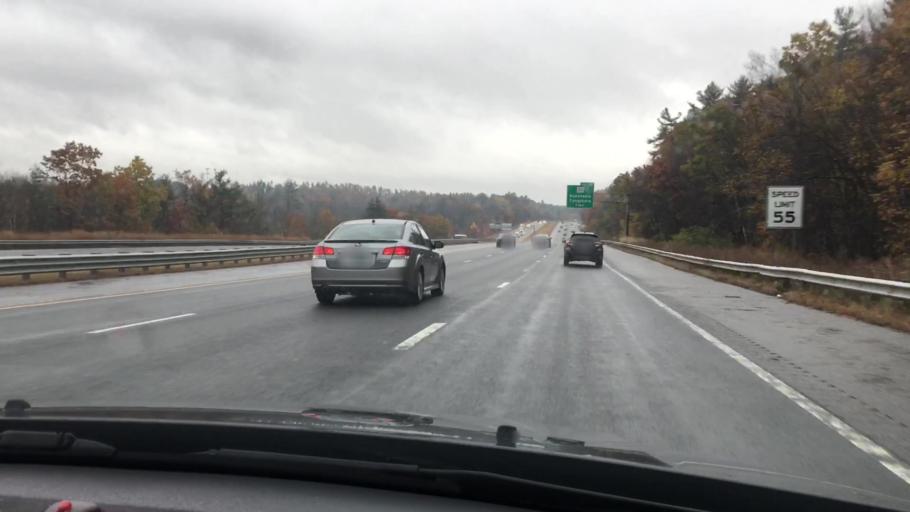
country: US
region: Massachusetts
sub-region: Middlesex County
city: Tyngsboro
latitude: 42.6989
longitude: -71.4488
